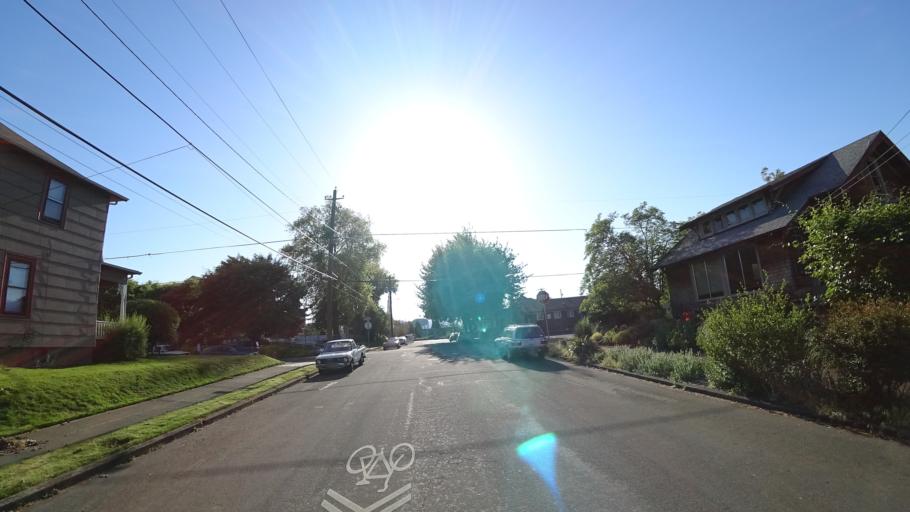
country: US
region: Oregon
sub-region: Multnomah County
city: Portland
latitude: 45.5569
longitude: -122.6767
